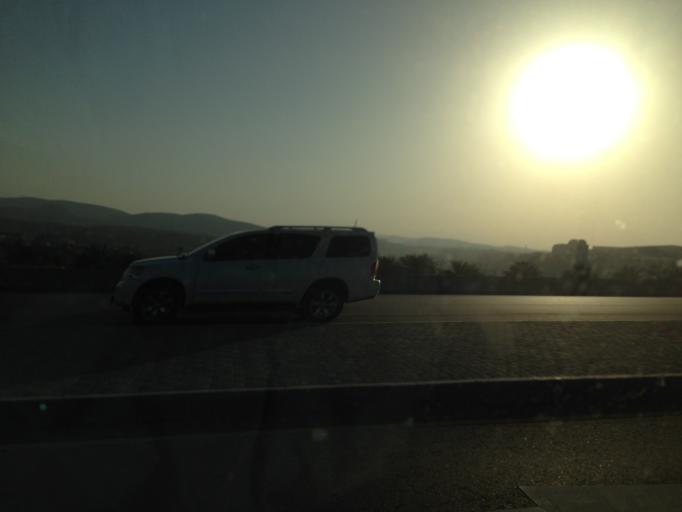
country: OM
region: Muhafazat Masqat
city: Bawshar
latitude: 23.5674
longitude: 58.3367
